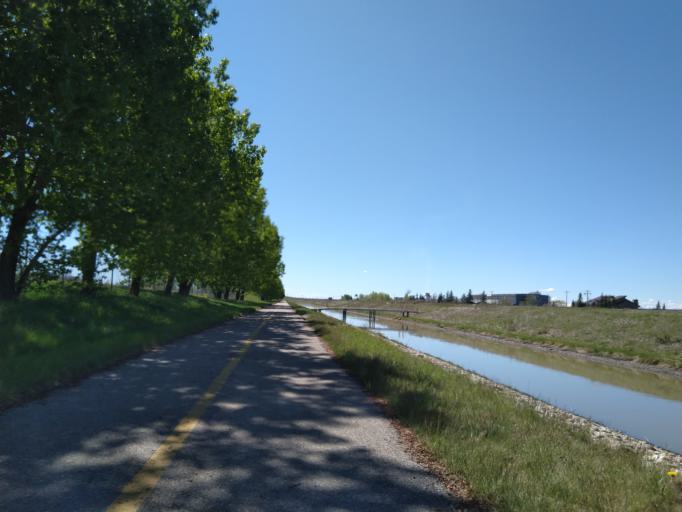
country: CA
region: Alberta
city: Calgary
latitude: 50.9751
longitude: -113.9914
